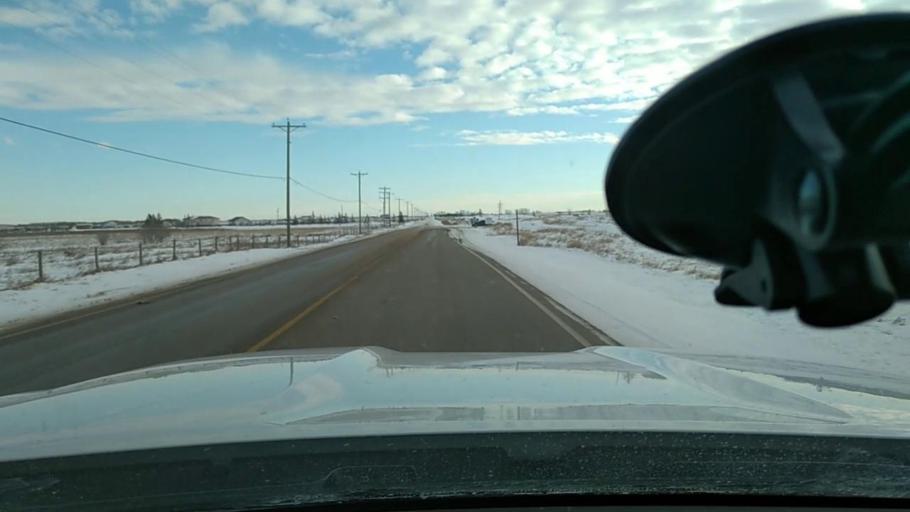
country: CA
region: Alberta
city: Chestermere
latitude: 50.9652
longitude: -113.6651
